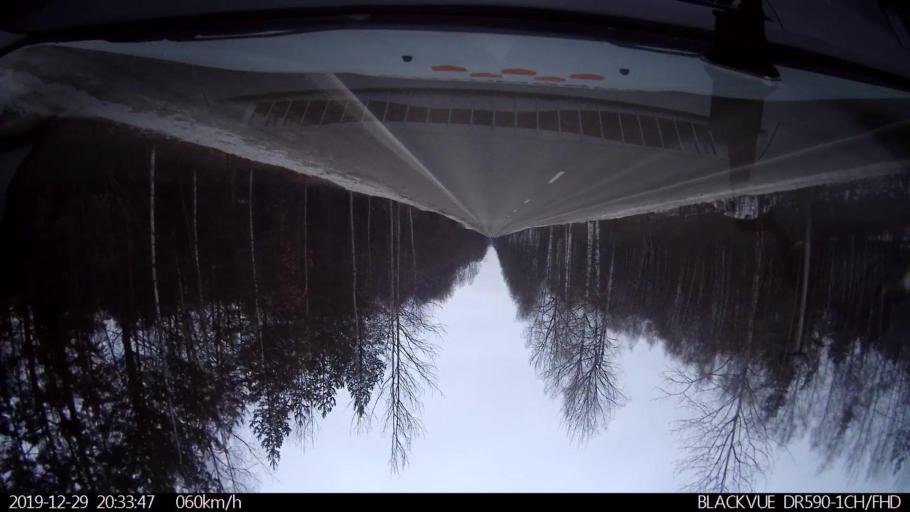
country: RU
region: Nizjnij Novgorod
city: Afonino
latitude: 56.1824
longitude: 44.0476
